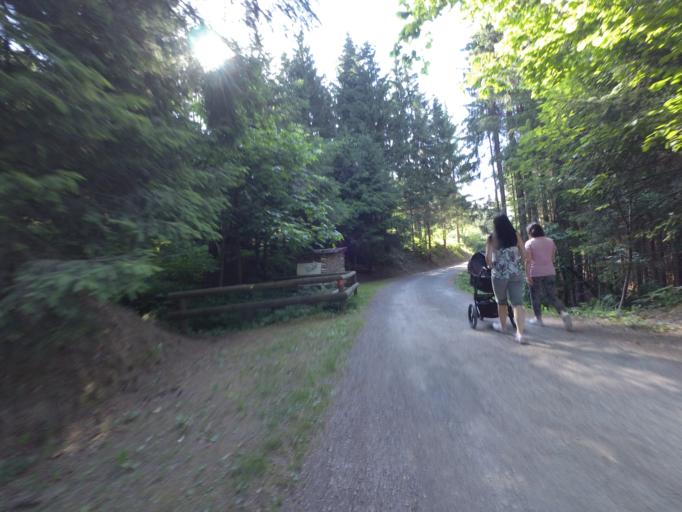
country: AT
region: Carinthia
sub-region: Politischer Bezirk Spittal an der Drau
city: Seeboden
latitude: 46.8075
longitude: 13.5236
